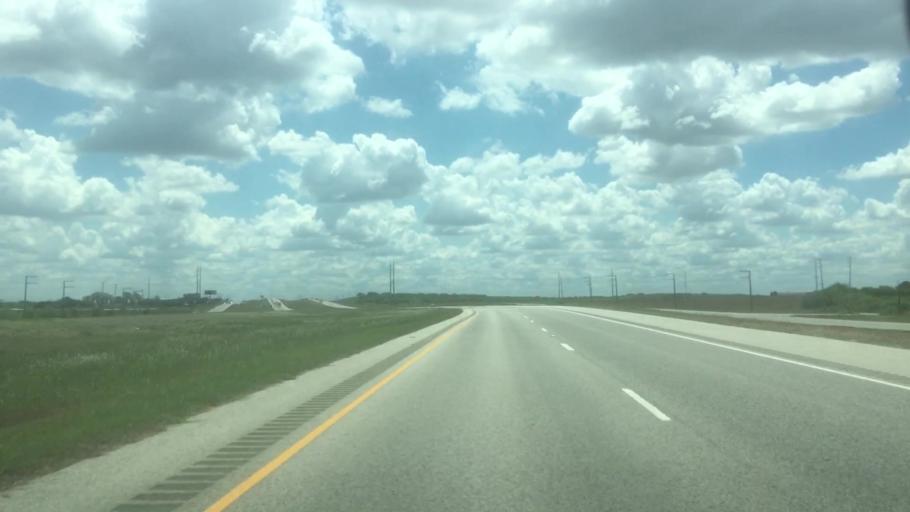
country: US
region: Texas
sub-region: Caldwell County
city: Uhland
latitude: 30.0174
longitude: -97.6881
